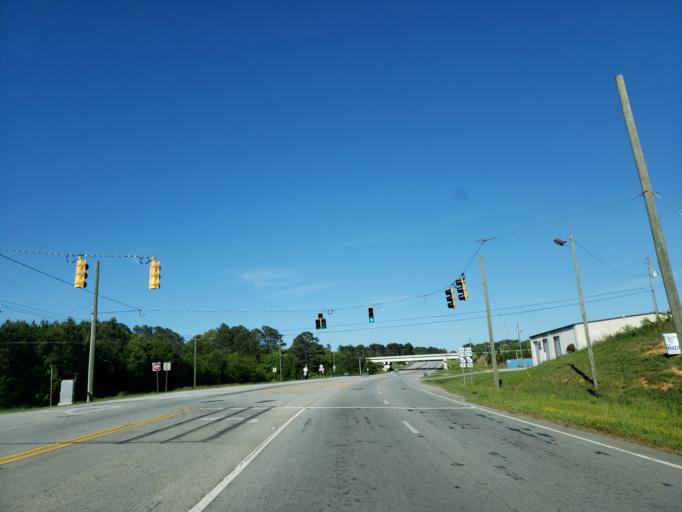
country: US
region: Georgia
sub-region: Polk County
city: Cedartown
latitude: 34.0159
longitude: -85.2242
